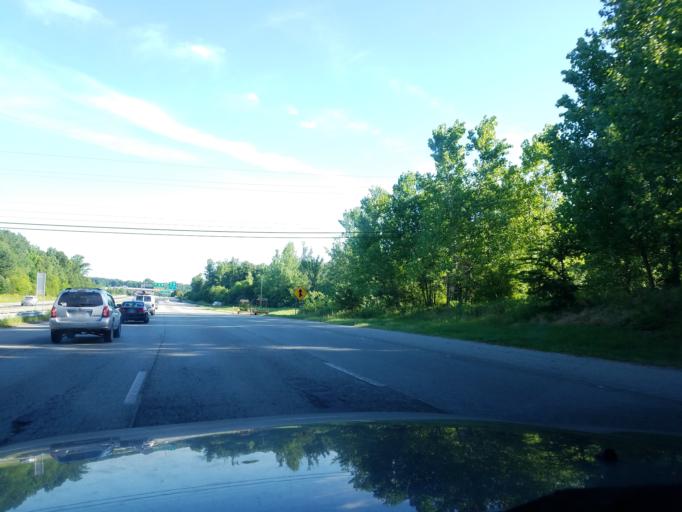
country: US
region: North Carolina
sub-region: Durham County
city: Durham
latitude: 36.0070
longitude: -78.8653
